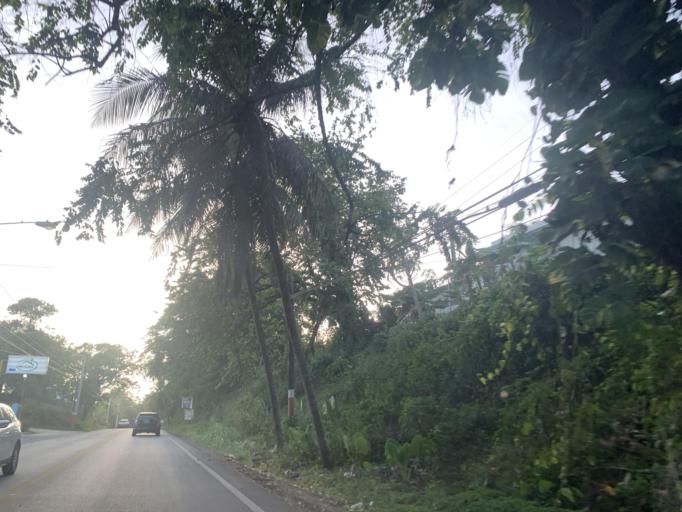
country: DO
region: Puerto Plata
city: Cabarete
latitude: 19.7748
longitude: -70.4466
